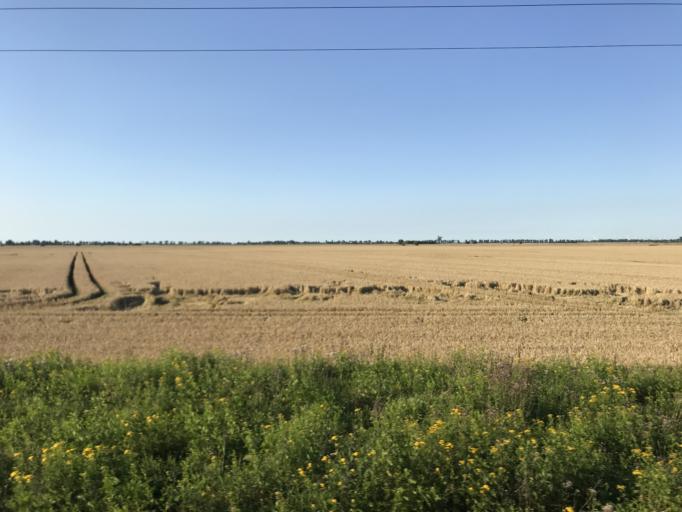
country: PL
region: Pomeranian Voivodeship
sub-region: Powiat malborski
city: Lisewo Malborskie
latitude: 54.0880
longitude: 18.8547
